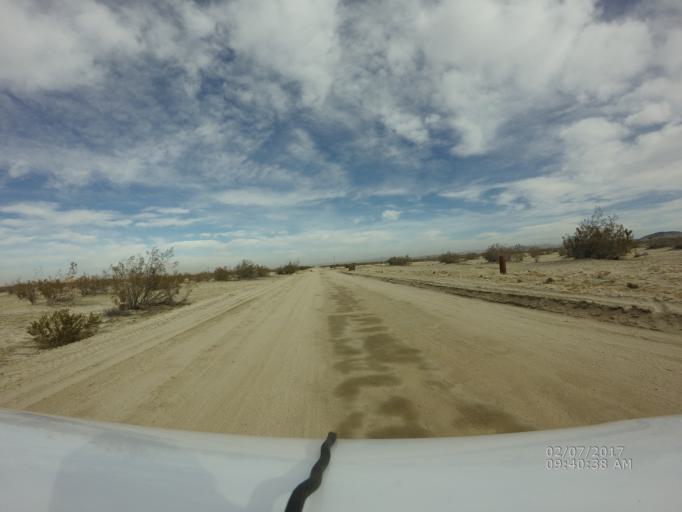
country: US
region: California
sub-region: Los Angeles County
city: Lake Los Angeles
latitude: 34.5622
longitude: -117.7114
